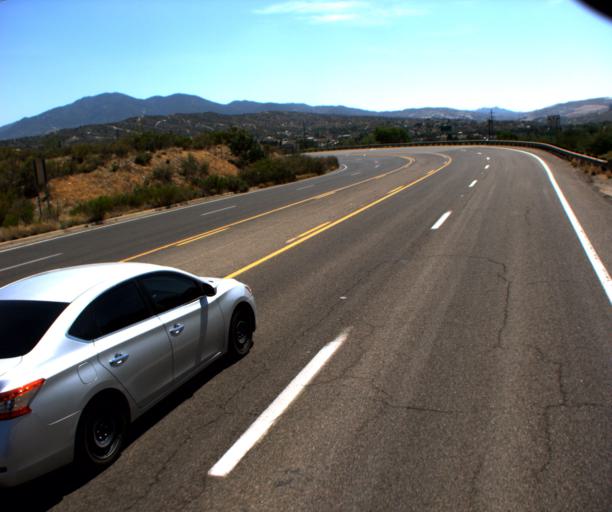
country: US
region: Arizona
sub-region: Gila County
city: Claypool
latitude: 33.4176
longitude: -110.8277
